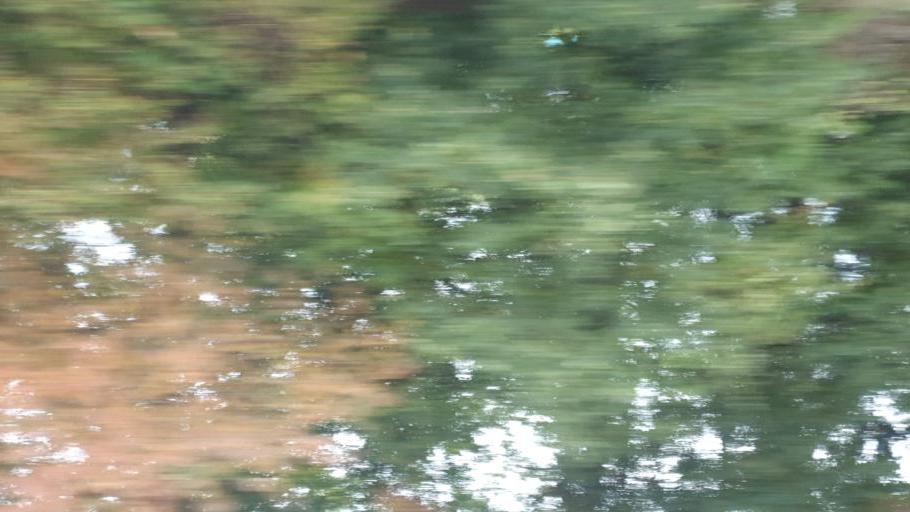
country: DE
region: Saarland
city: Sankt Ingbert
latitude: 49.2771
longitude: 7.1560
